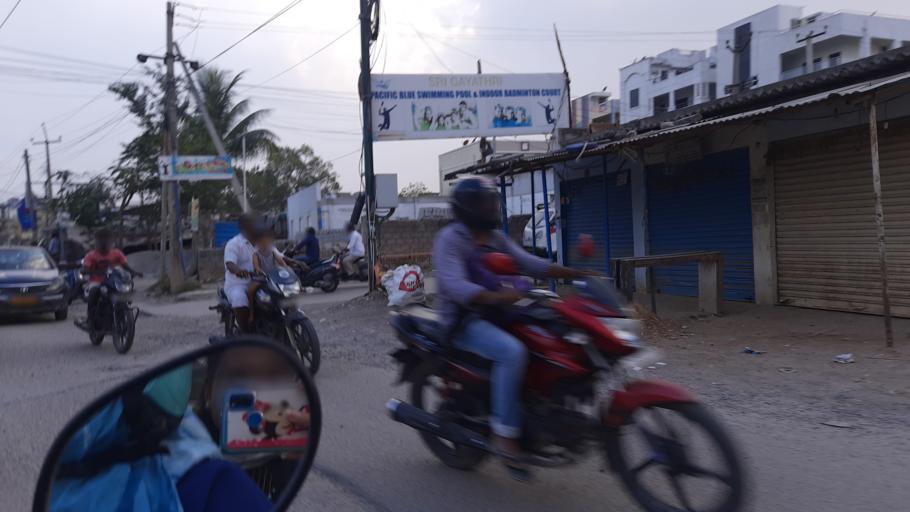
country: IN
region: Telangana
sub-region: Rangareddi
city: Kukatpalli
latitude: 17.4951
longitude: 78.4202
